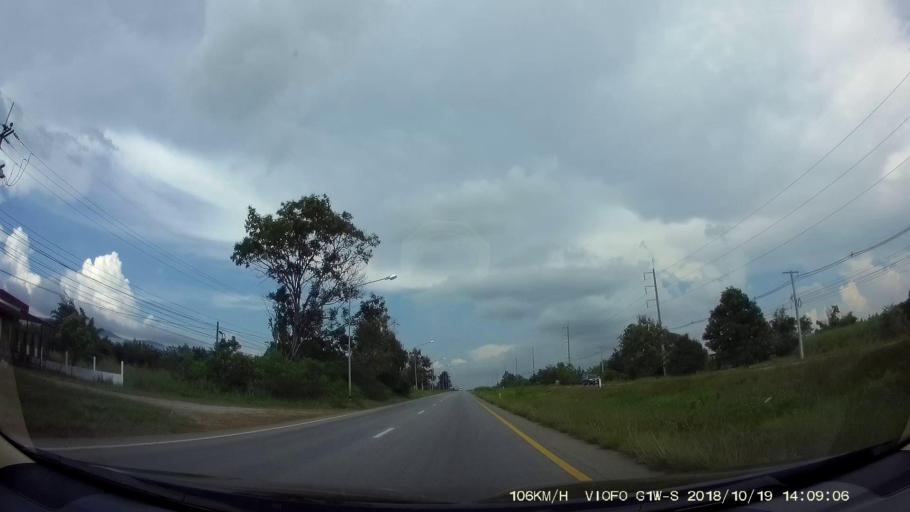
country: TH
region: Chaiyaphum
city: Chaiyaphum
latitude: 15.9147
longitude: 102.1314
